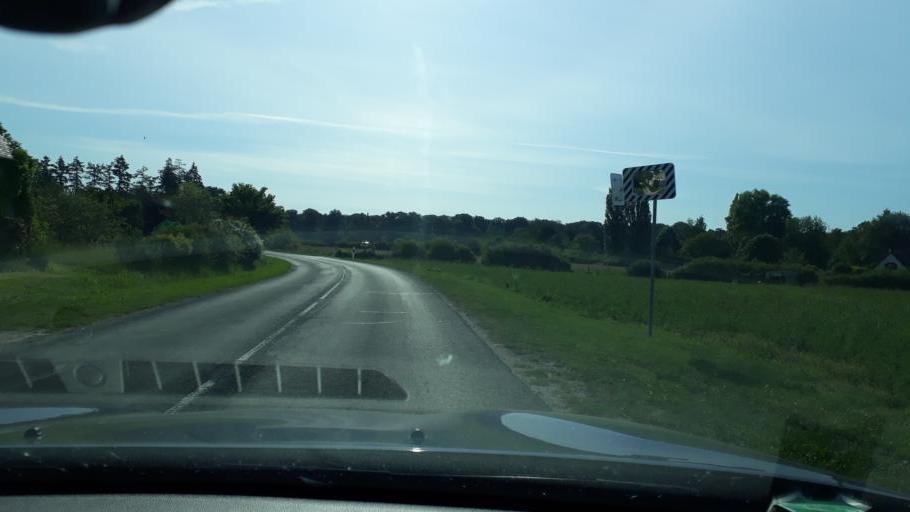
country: FR
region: Centre
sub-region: Departement du Loiret
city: Chilleurs-aux-Bois
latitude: 48.0649
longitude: 2.2199
